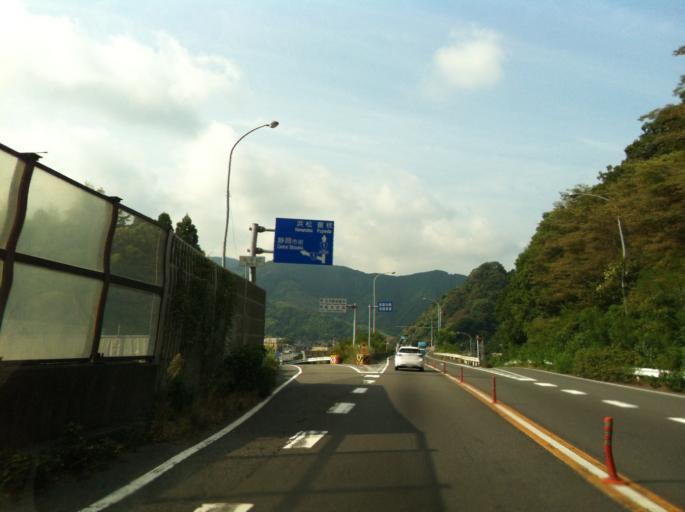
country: JP
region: Shizuoka
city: Shizuoka-shi
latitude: 34.9527
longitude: 138.3336
